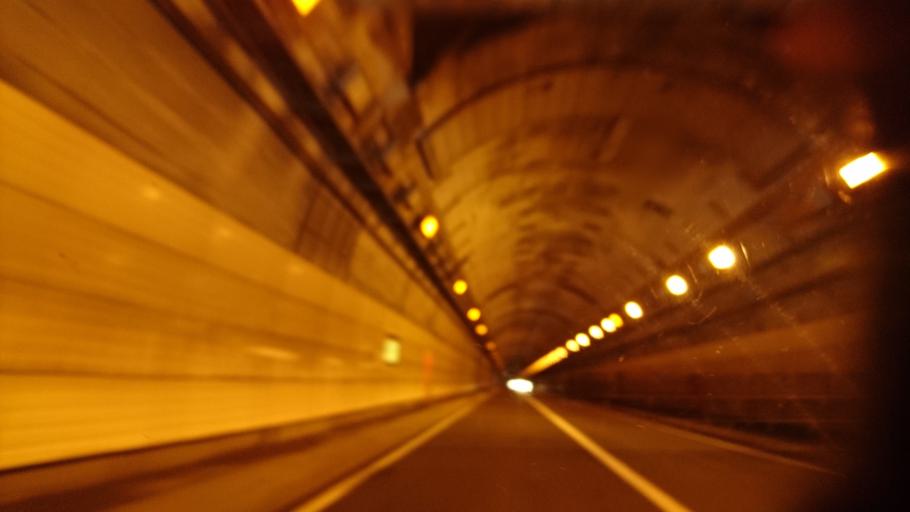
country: JP
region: Iwate
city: Shizukuishi
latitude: 39.6978
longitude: 140.8011
